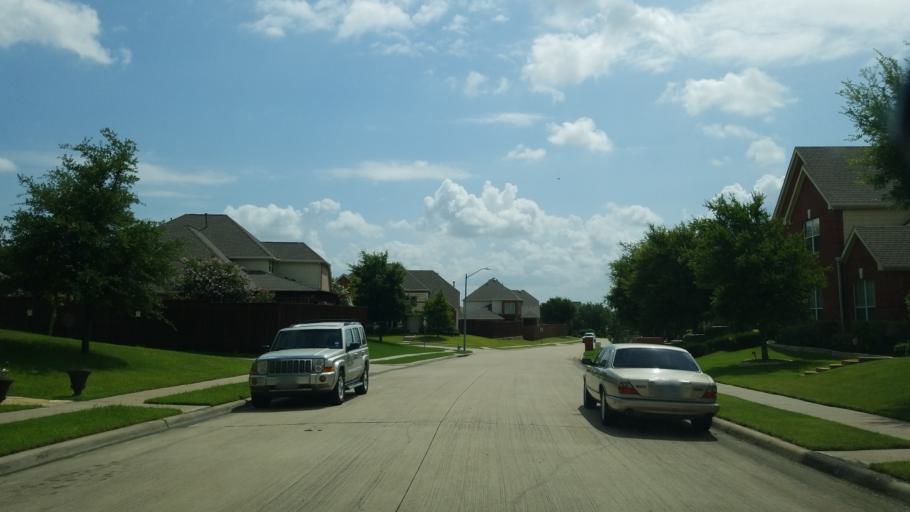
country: US
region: Texas
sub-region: Dallas County
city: Coppell
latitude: 32.9277
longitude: -96.9636
